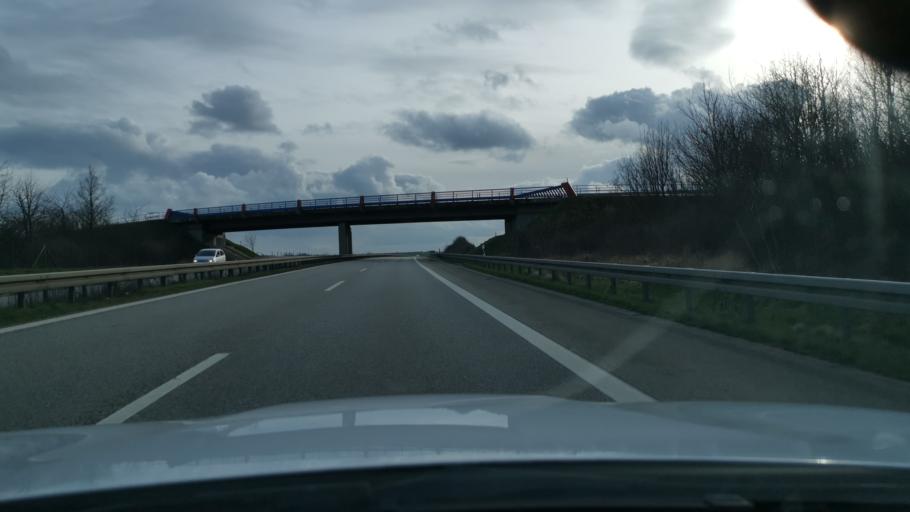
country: DE
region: Mecklenburg-Vorpommern
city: Kritzmow
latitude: 54.0661
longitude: 12.0484
